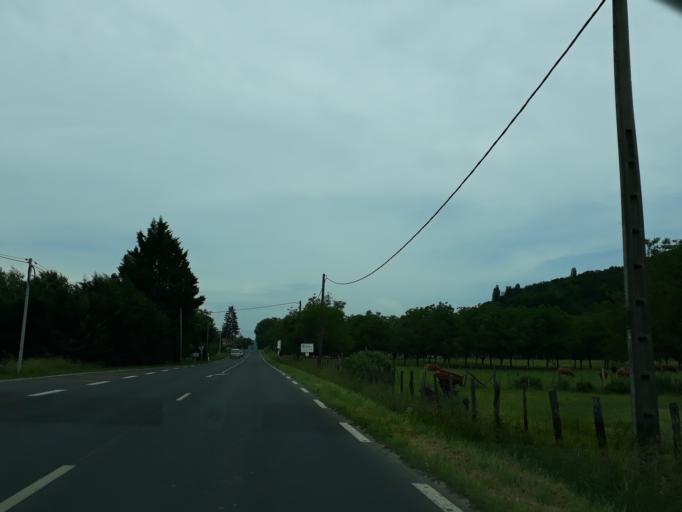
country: FR
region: Limousin
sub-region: Departement de la Correze
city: Mansac
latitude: 45.1272
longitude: 1.3541
